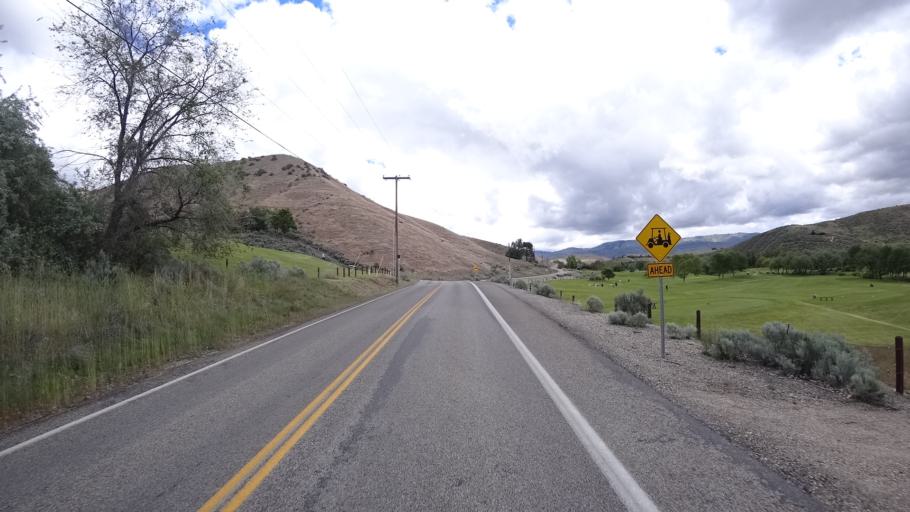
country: US
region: Idaho
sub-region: Ada County
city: Garden City
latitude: 43.6598
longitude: -116.2305
